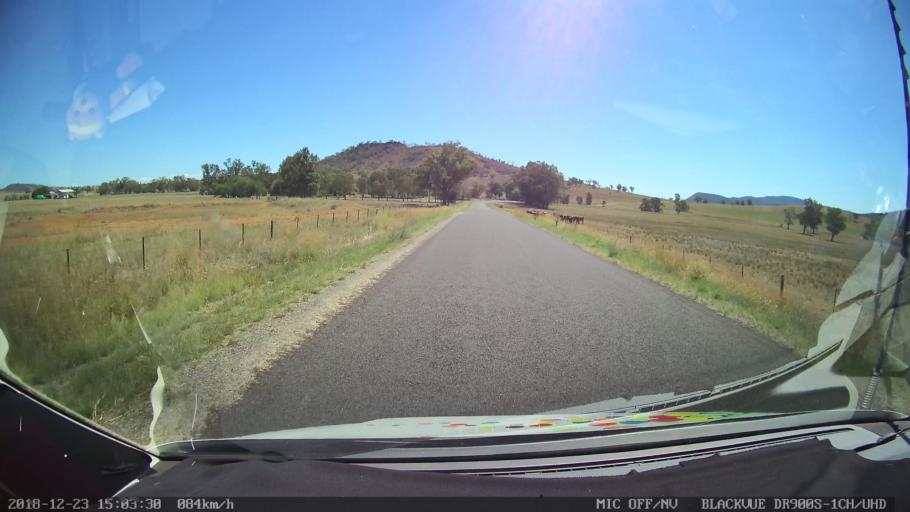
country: AU
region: New South Wales
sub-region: Tamworth Municipality
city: Manilla
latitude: -30.7391
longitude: 150.7643
